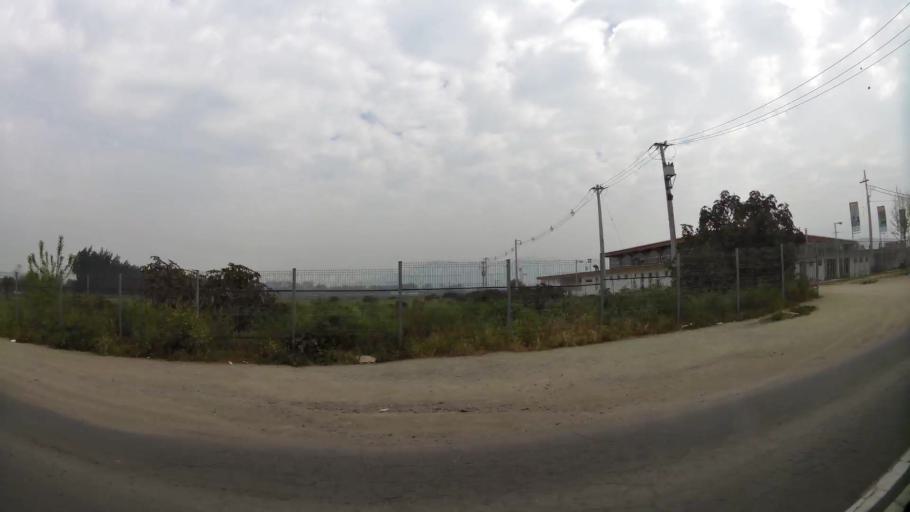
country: CL
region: Santiago Metropolitan
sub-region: Provincia de Chacabuco
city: Chicureo Abajo
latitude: -33.2085
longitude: -70.6848
